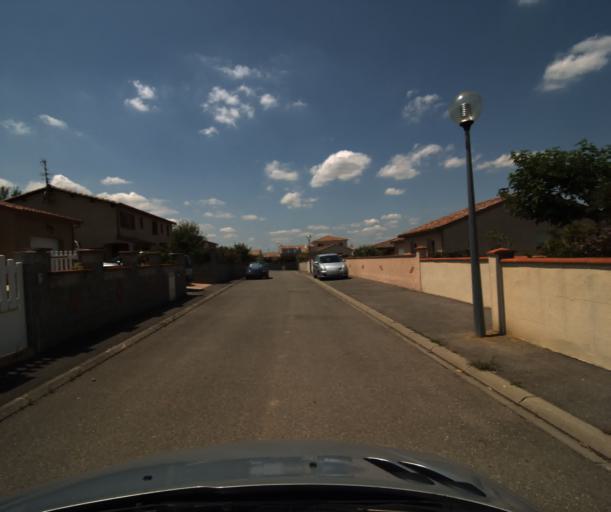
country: FR
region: Midi-Pyrenees
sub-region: Departement de la Haute-Garonne
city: Saint-Lys
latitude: 43.5145
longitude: 1.1903
